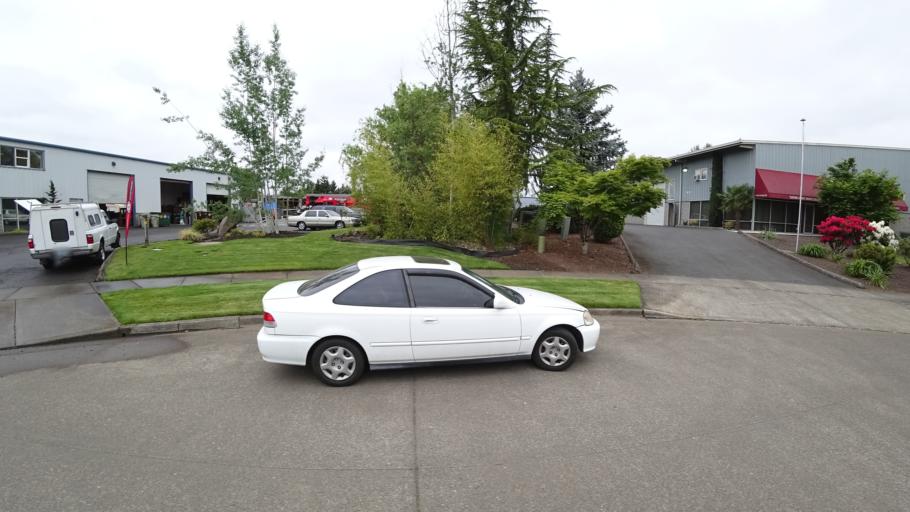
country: US
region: Oregon
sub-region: Washington County
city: Aloha
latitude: 45.4964
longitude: -122.9203
